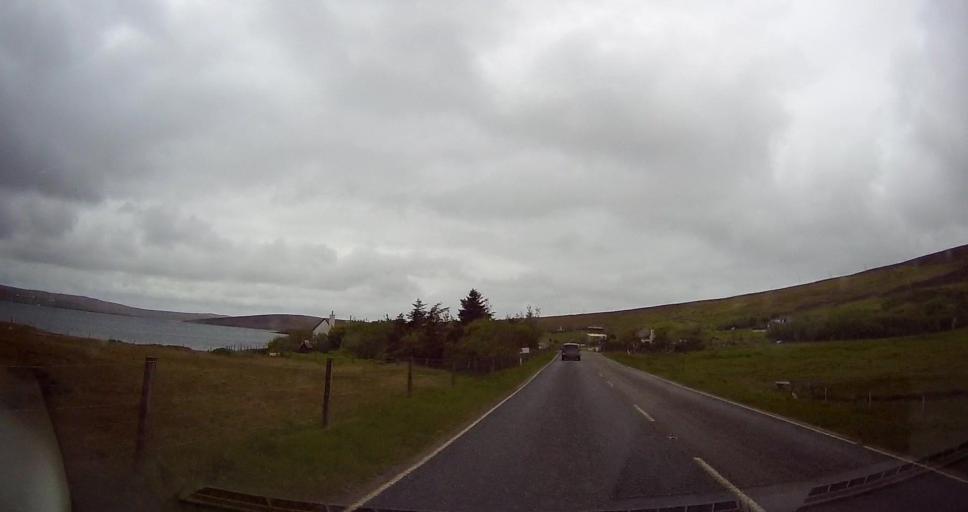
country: GB
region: Scotland
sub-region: Shetland Islands
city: Lerwick
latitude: 60.2444
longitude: -1.3525
